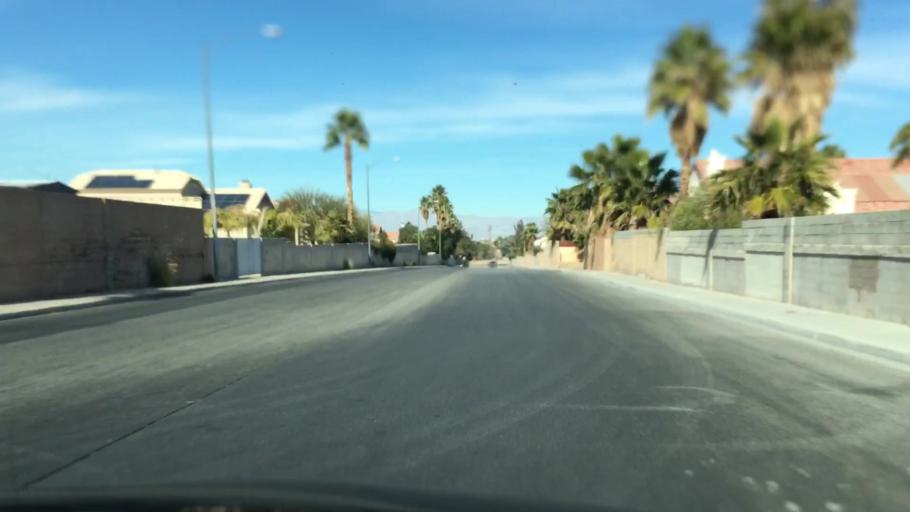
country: US
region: Nevada
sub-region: Clark County
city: Paradise
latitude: 36.0387
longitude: -115.1407
